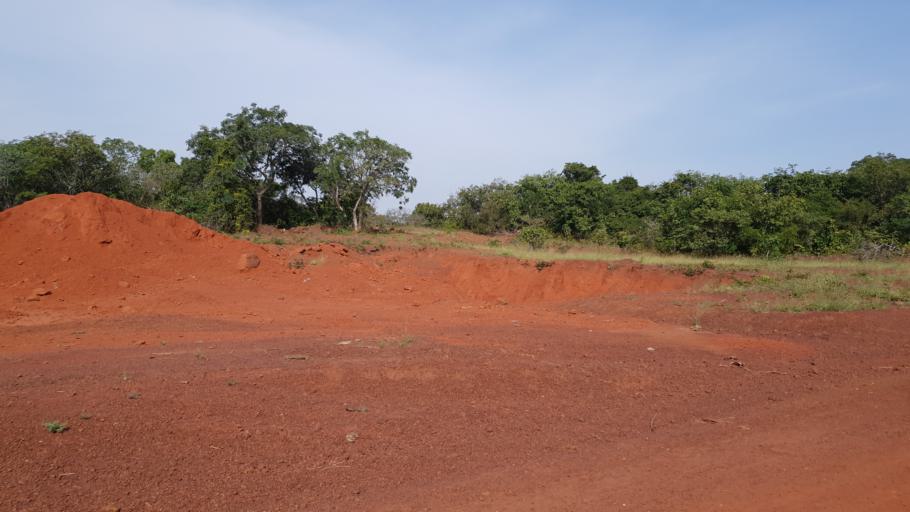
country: ML
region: Sikasso
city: Sikasso
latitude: 11.6960
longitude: -6.2727
